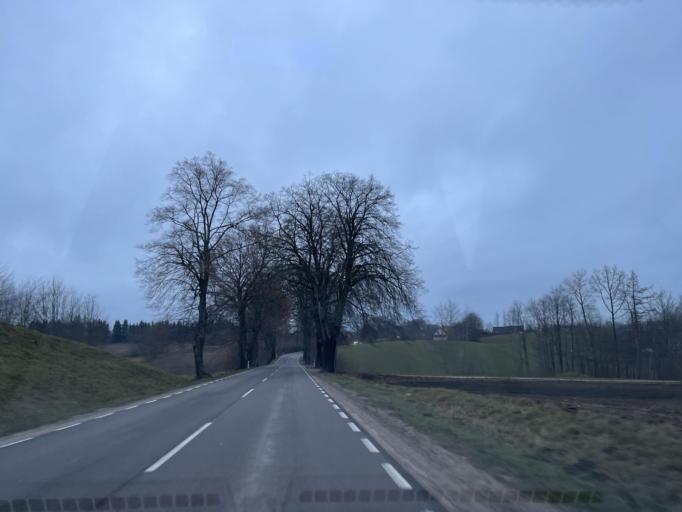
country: PL
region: Pomeranian Voivodeship
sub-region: Powiat kartuski
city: Przodkowo
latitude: 54.3971
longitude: 18.2334
